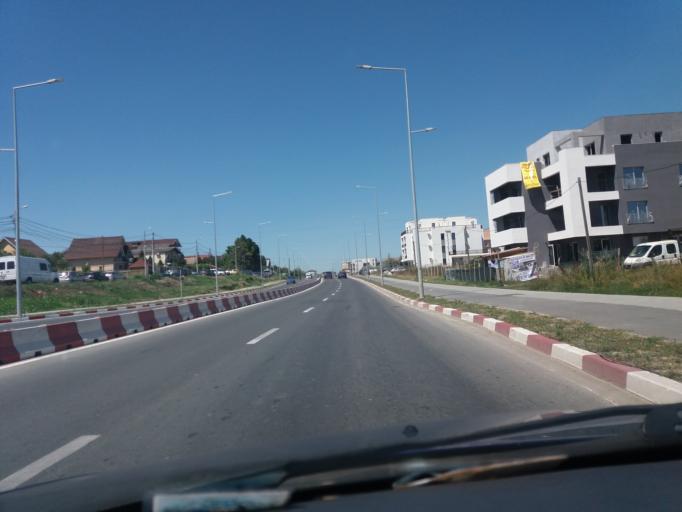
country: RO
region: Constanta
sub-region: Comuna Navodari
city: Navodari
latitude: 44.2919
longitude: 28.6194
